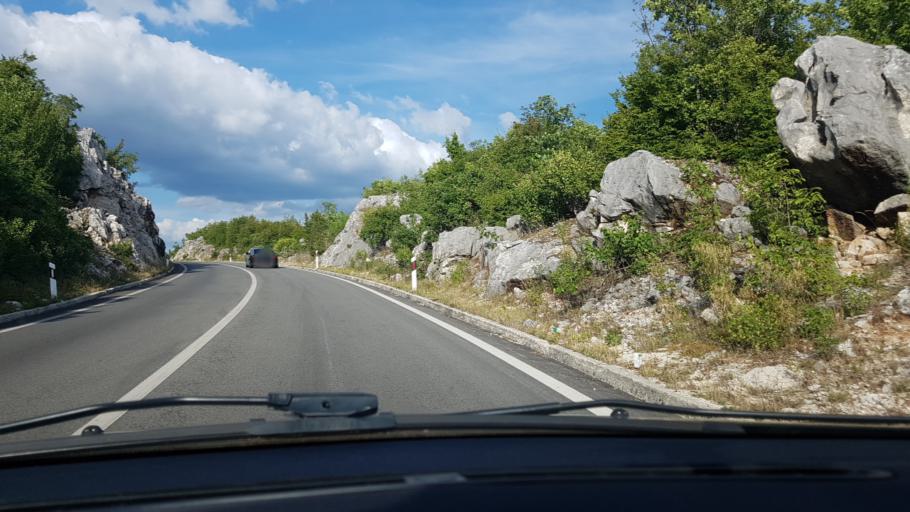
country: HR
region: Splitsko-Dalmatinska
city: Grubine
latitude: 43.4060
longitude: 17.0841
